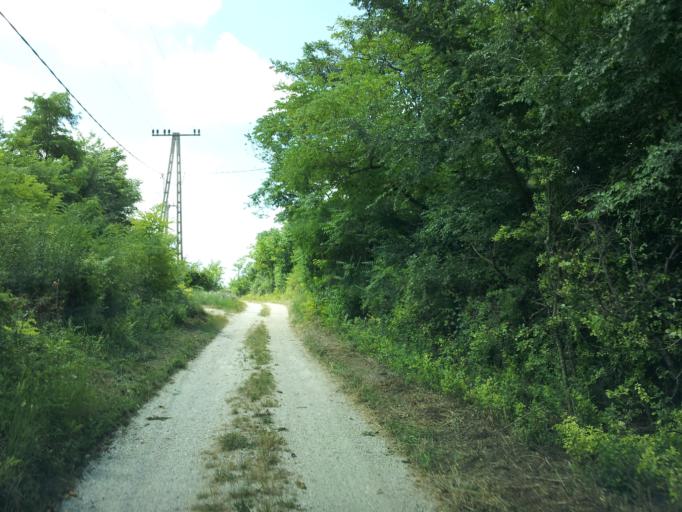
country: HU
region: Veszprem
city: Balatonkenese
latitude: 47.0421
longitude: 18.0910
